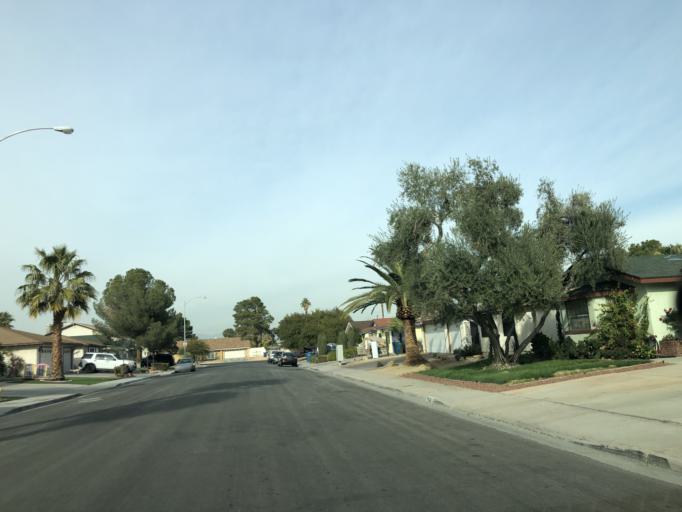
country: US
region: Nevada
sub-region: Clark County
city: Winchester
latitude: 36.1173
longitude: -115.1239
